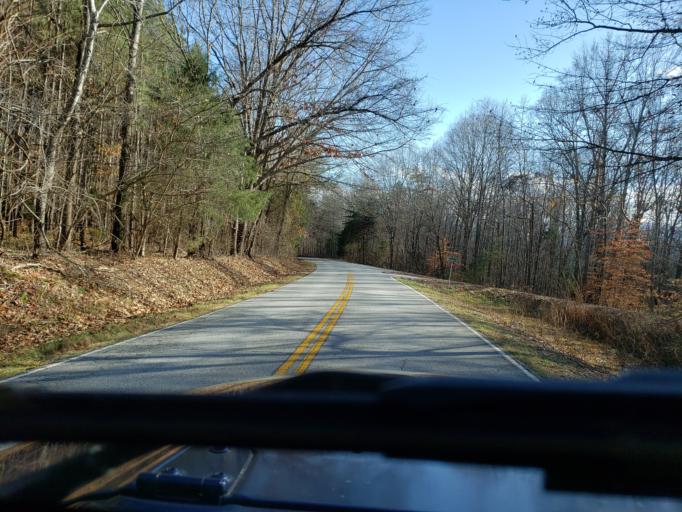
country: US
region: North Carolina
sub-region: Cleveland County
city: White Plains
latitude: 35.1594
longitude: -81.4048
